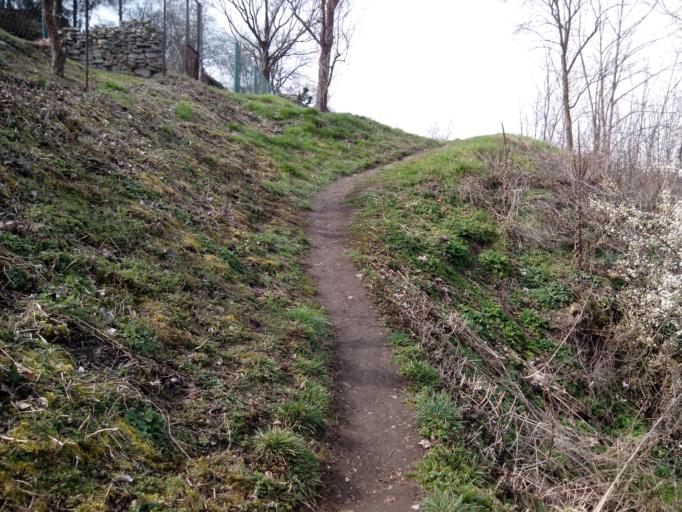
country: CZ
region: Central Bohemia
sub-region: Okres Beroun
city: Beroun
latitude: 49.9500
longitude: 14.1056
